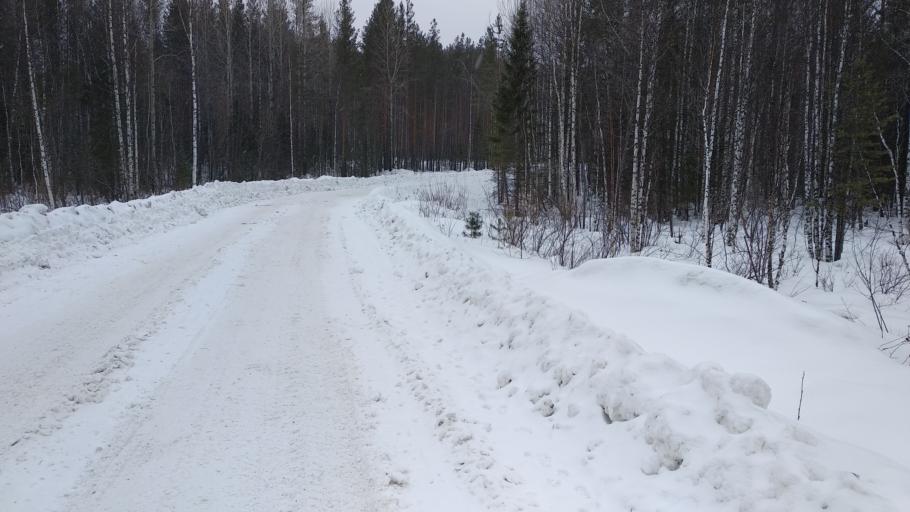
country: RU
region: Sverdlovsk
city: Karpinsk
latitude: 59.6984
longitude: 59.6064
